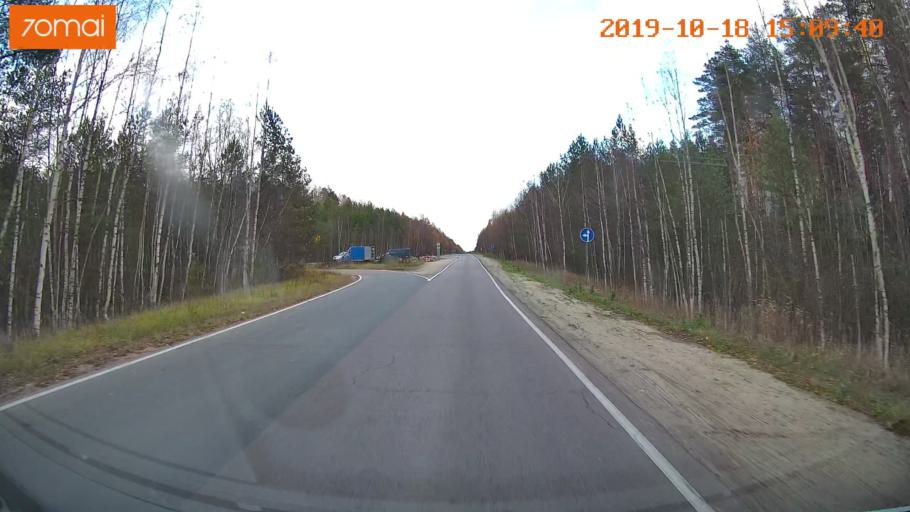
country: RU
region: Vladimir
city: Gus'-Khrustal'nyy
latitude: 55.5674
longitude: 40.6240
